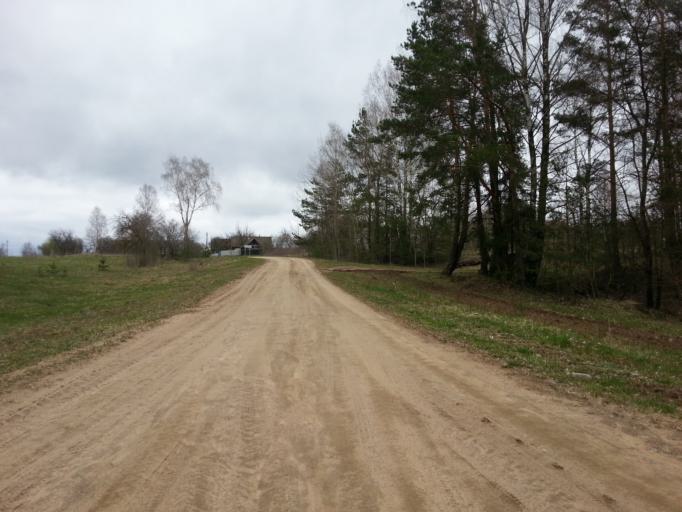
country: BY
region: Minsk
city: Horad Barysaw
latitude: 54.4237
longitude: 28.4665
